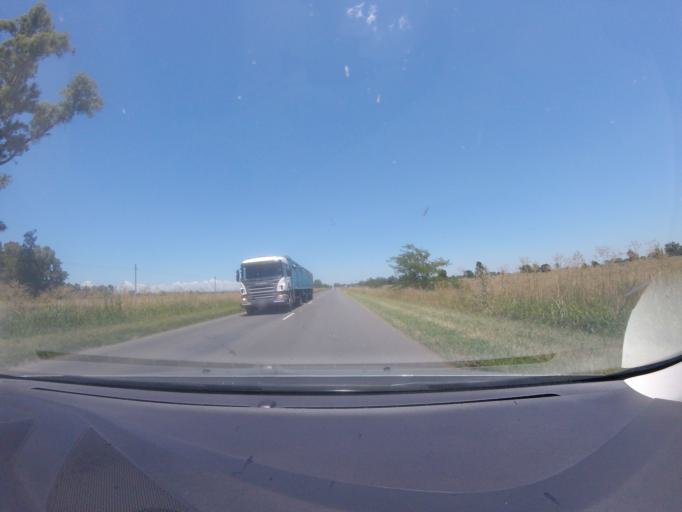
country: AR
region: Buenos Aires
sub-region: Partido de Rauch
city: Rauch
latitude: -36.7557
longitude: -59.0796
